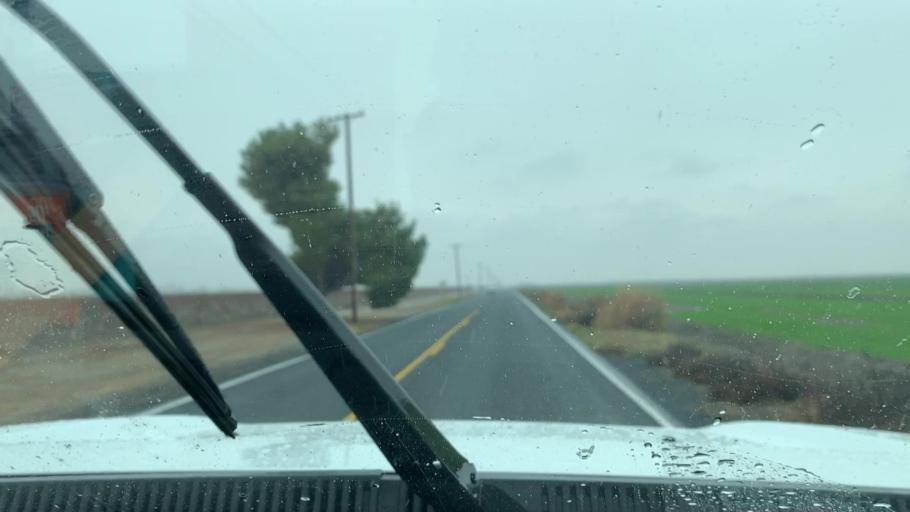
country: US
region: California
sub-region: Tulare County
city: Earlimart
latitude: 35.8917
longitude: -119.3765
